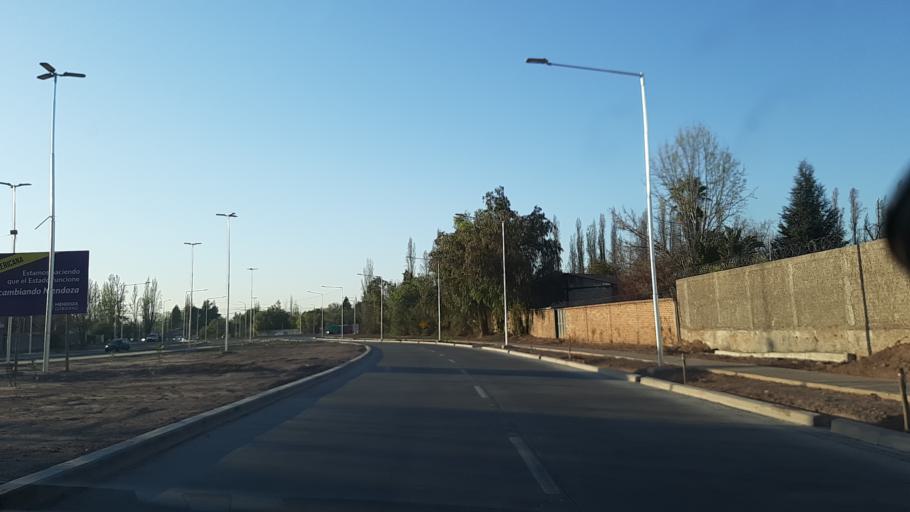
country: AR
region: Mendoza
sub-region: Departamento de Godoy Cruz
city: Godoy Cruz
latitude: -32.9628
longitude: -68.8633
